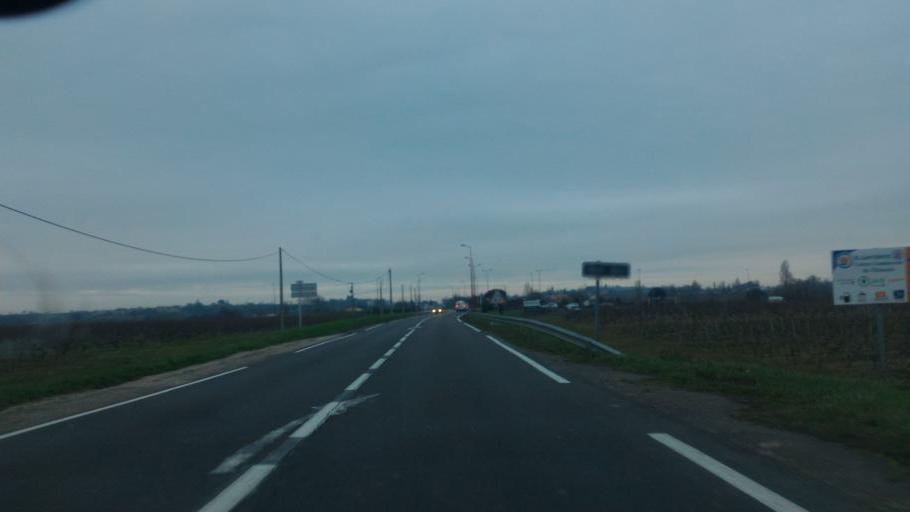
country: FR
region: Aquitaine
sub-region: Departement de la Gironde
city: Berson
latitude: 45.1243
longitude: -0.5925
